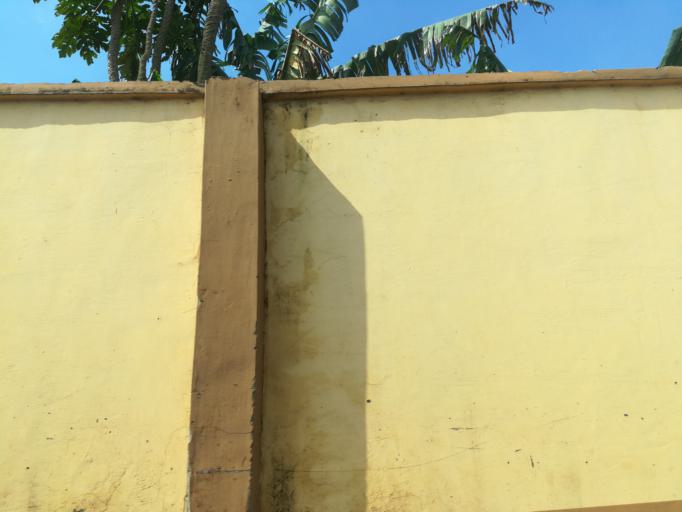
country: NG
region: Lagos
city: Ikorodu
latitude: 6.5955
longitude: 3.5178
